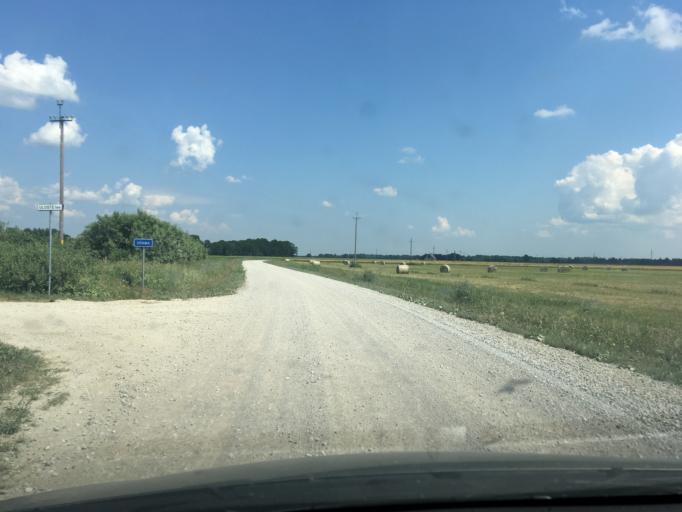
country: EE
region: Laeaene
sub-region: Lihula vald
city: Lihula
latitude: 58.7151
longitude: 24.0706
